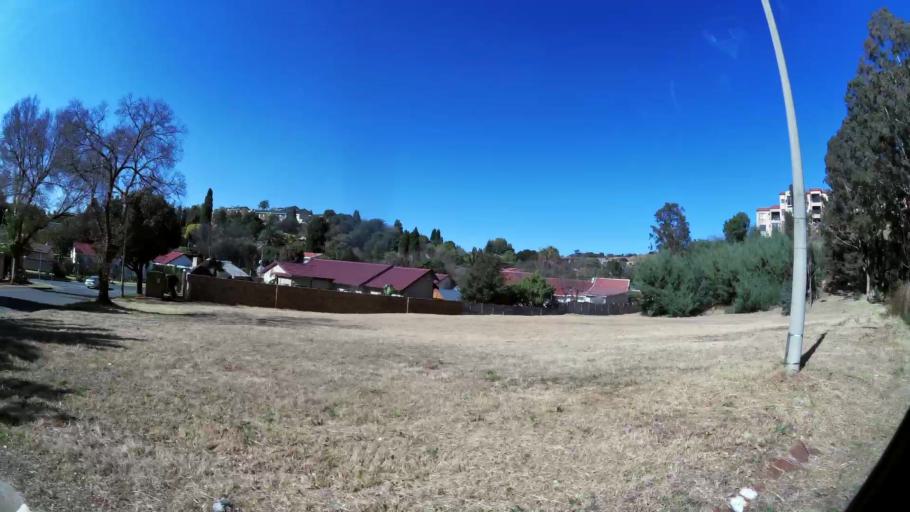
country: ZA
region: Gauteng
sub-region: City of Johannesburg Metropolitan Municipality
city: Roodepoort
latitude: -26.1166
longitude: 27.8576
